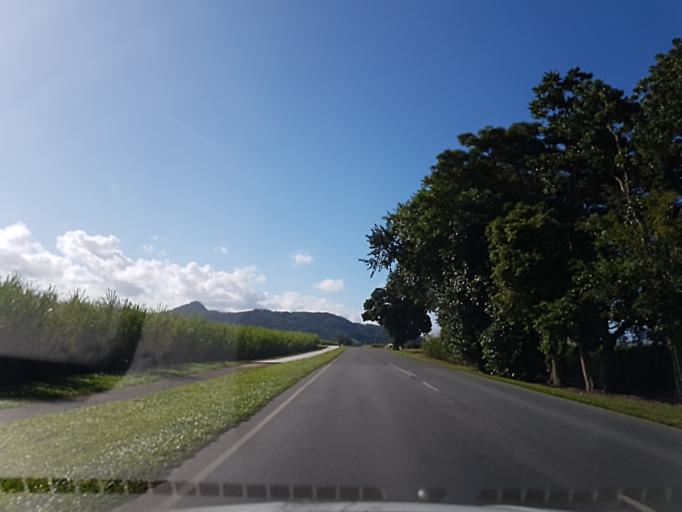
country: AU
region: Queensland
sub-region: Cairns
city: Port Douglas
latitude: -16.4488
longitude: 145.3721
